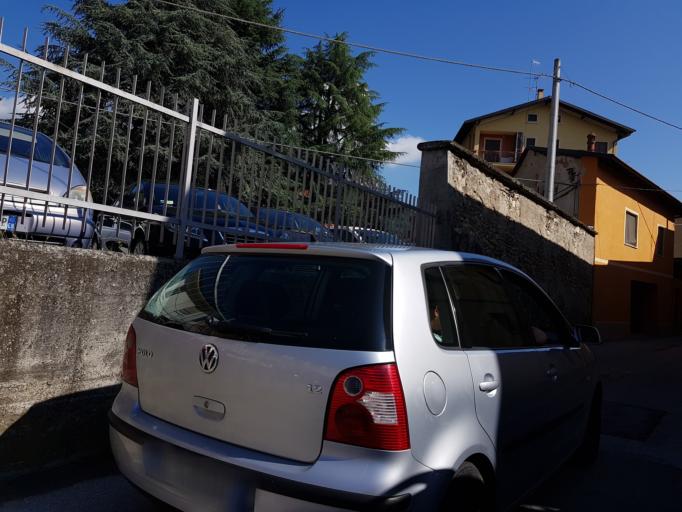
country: IT
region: Piedmont
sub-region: Provincia di Cuneo
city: Dronero
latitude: 44.4665
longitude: 7.3587
